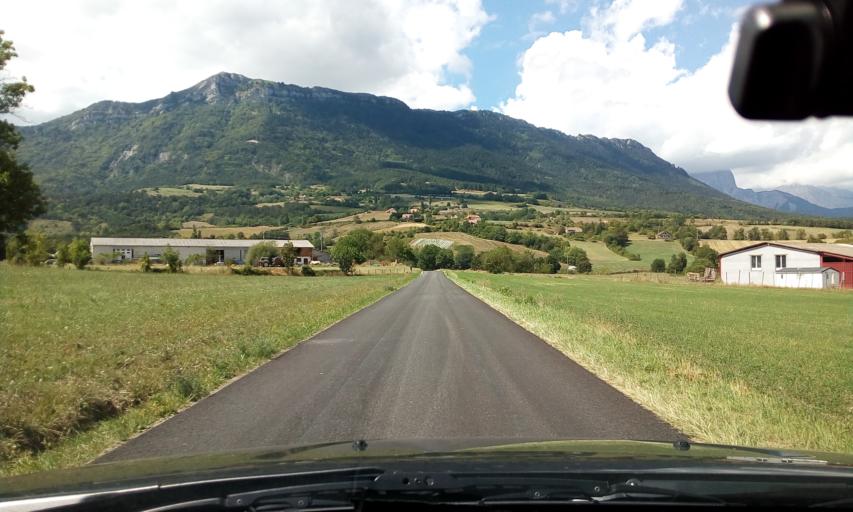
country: FR
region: Rhone-Alpes
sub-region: Departement de l'Isere
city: Mens
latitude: 44.7946
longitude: 5.6495
